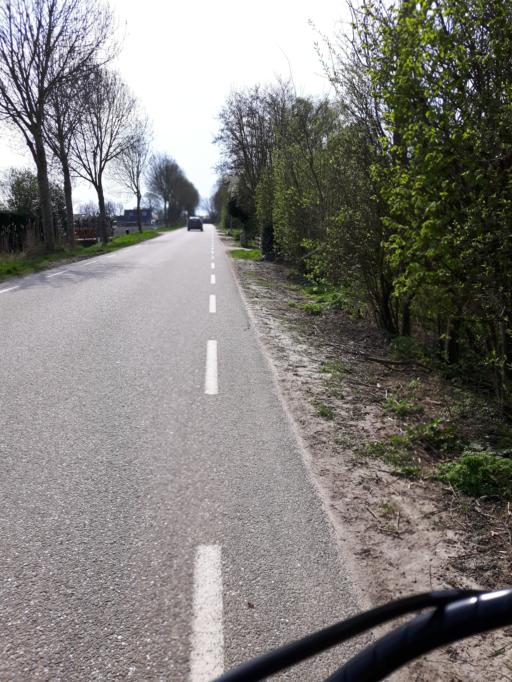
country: NL
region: Zeeland
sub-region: Gemeente Goes
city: Goes
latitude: 51.5060
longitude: 3.9492
